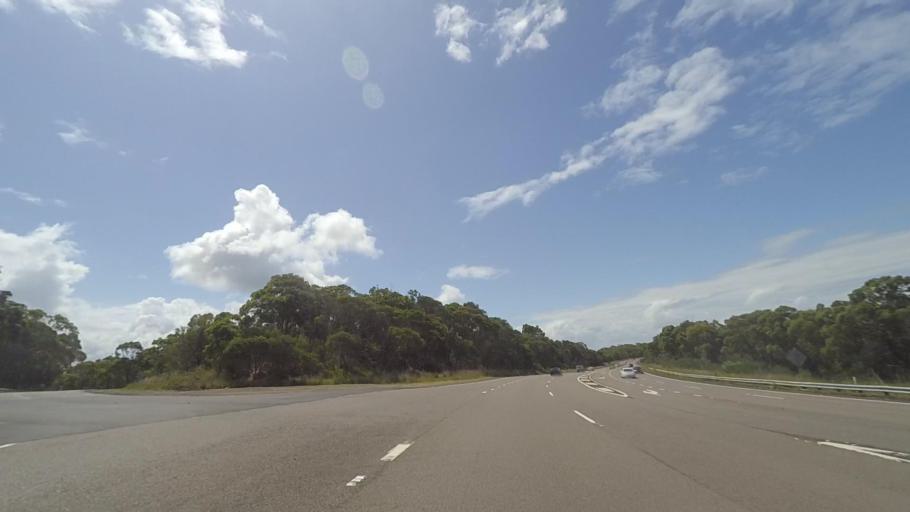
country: AU
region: New South Wales
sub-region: Wyong Shire
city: Kingfisher Shores
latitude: -33.1435
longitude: 151.6105
